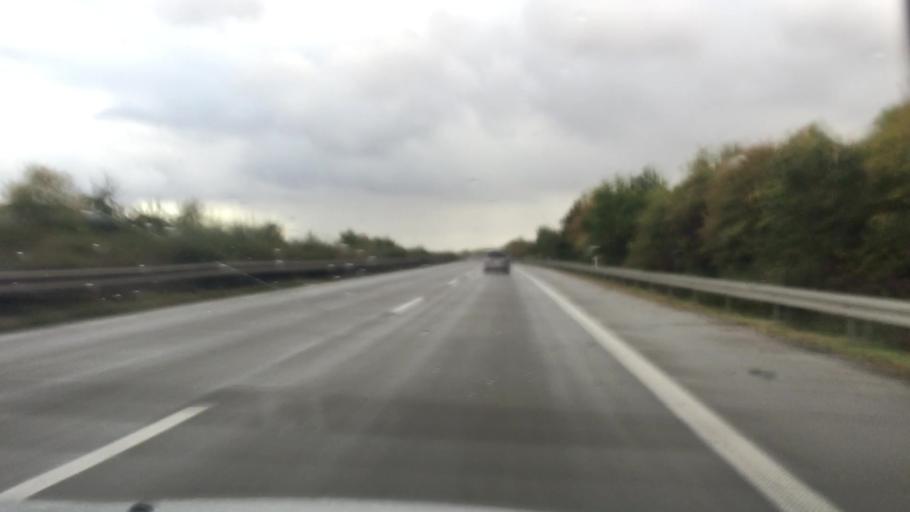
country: DE
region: Saxony-Anhalt
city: Hohendodeleben
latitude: 52.1099
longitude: 11.5276
